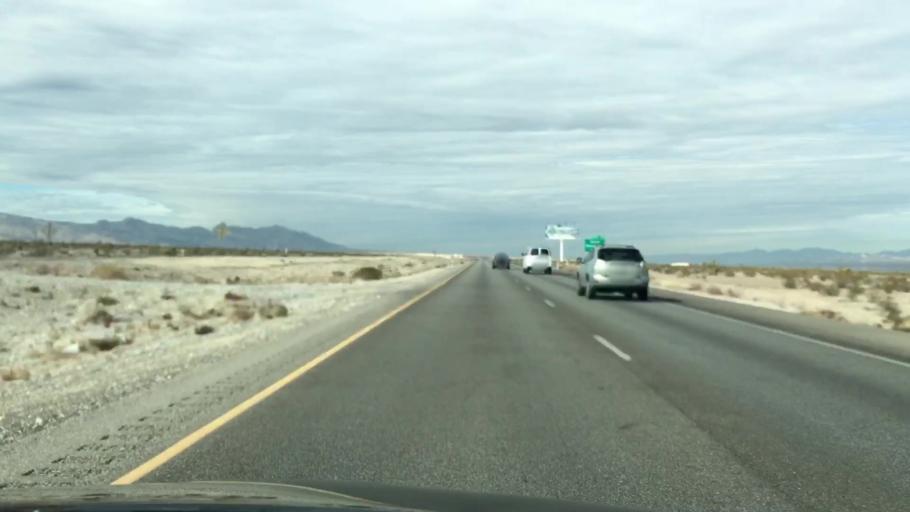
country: US
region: Nevada
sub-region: Clark County
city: Summerlin South
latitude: 36.3475
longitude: -115.3333
